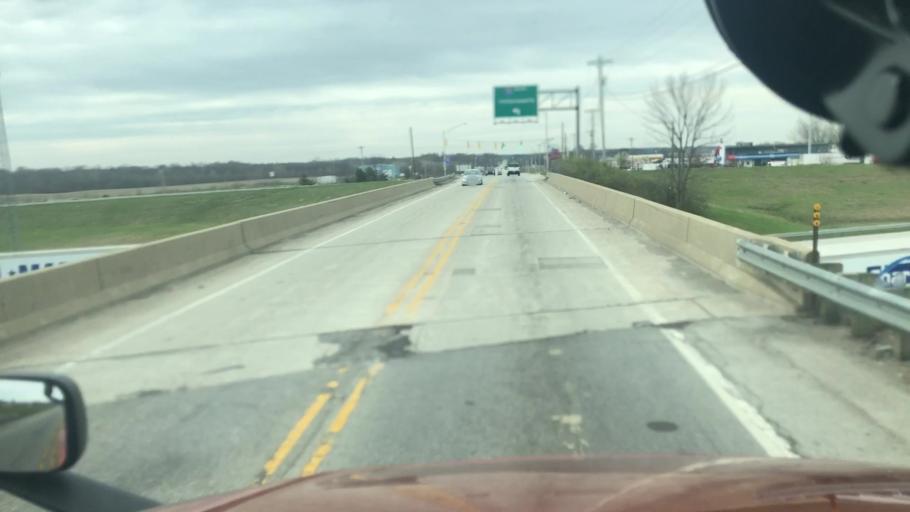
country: US
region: Indiana
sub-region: Morgan County
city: Monrovia
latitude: 39.6140
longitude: -86.4798
